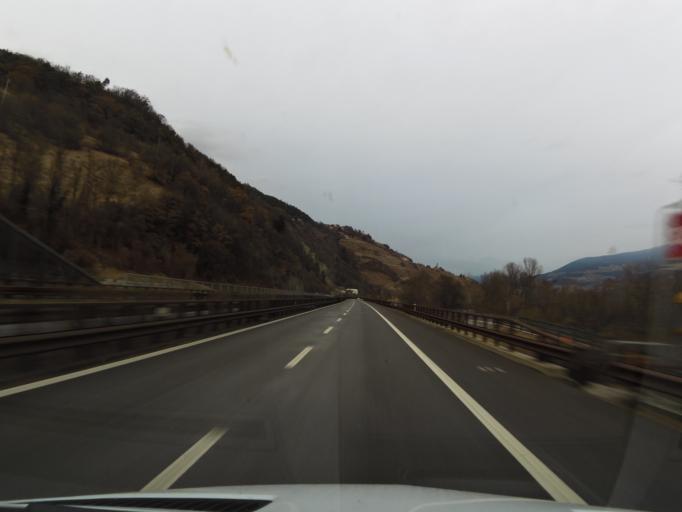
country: IT
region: Trentino-Alto Adige
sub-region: Bolzano
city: Velturno
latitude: 46.6785
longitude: 11.6219
